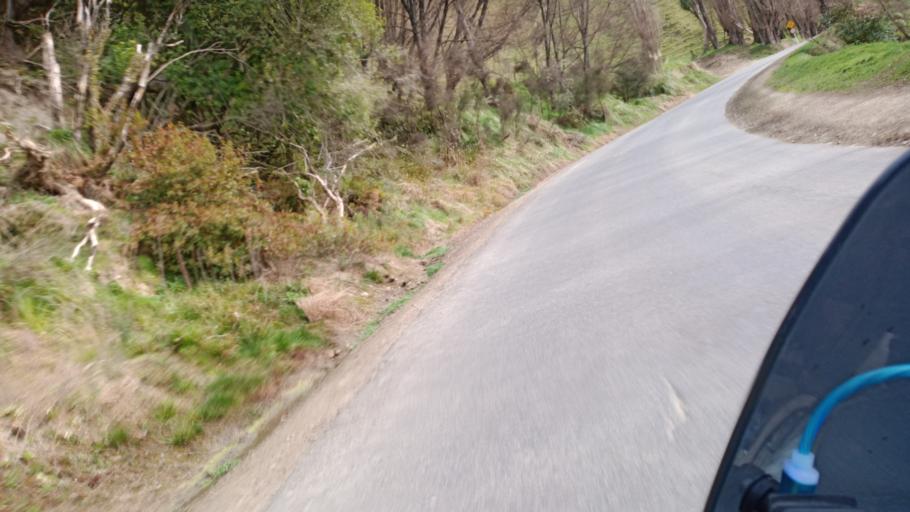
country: NZ
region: Hawke's Bay
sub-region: Wairoa District
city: Wairoa
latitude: -38.8031
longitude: 177.4473
